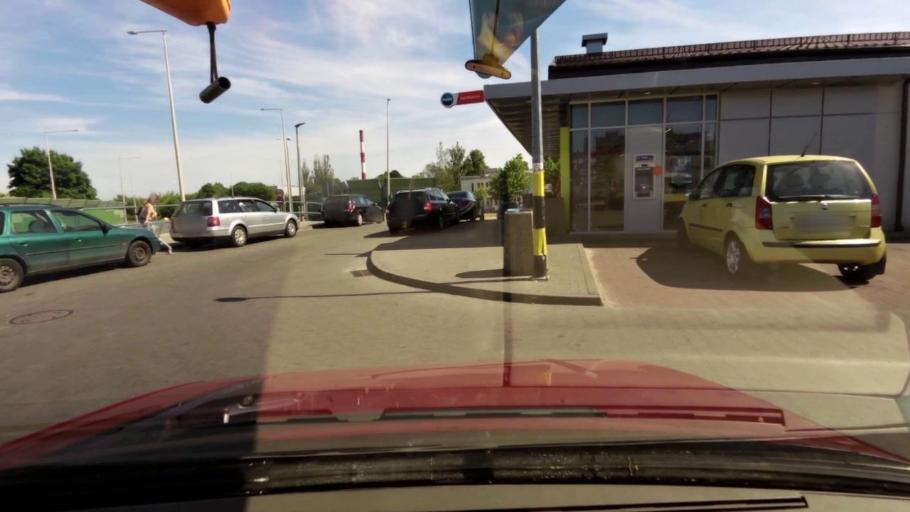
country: PL
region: Pomeranian Voivodeship
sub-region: Powiat slupski
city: Kobylnica
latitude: 54.4570
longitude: 16.9935
